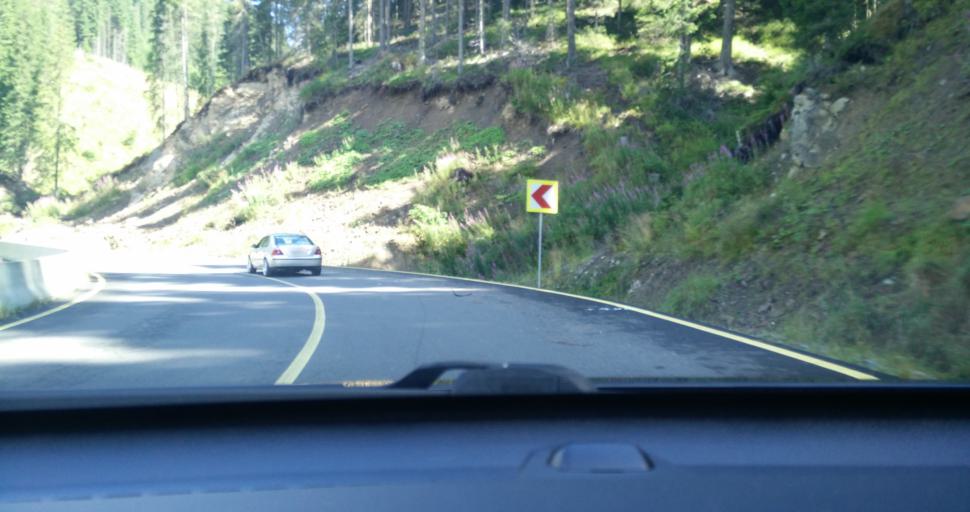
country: RO
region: Hunedoara
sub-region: Oras Petrila
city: Petrila
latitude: 45.4446
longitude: 23.6248
